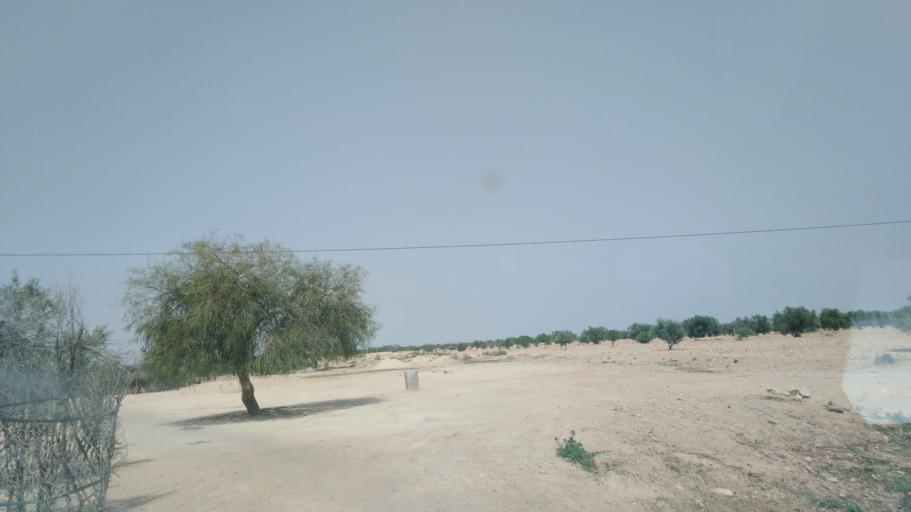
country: TN
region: Safaqis
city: Sfax
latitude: 34.6559
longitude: 10.5546
